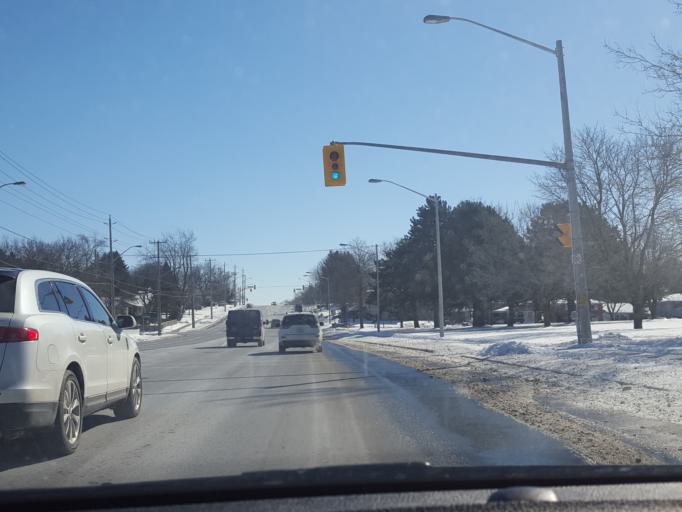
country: CA
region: Ontario
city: Kitchener
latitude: 43.4258
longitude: -80.5215
